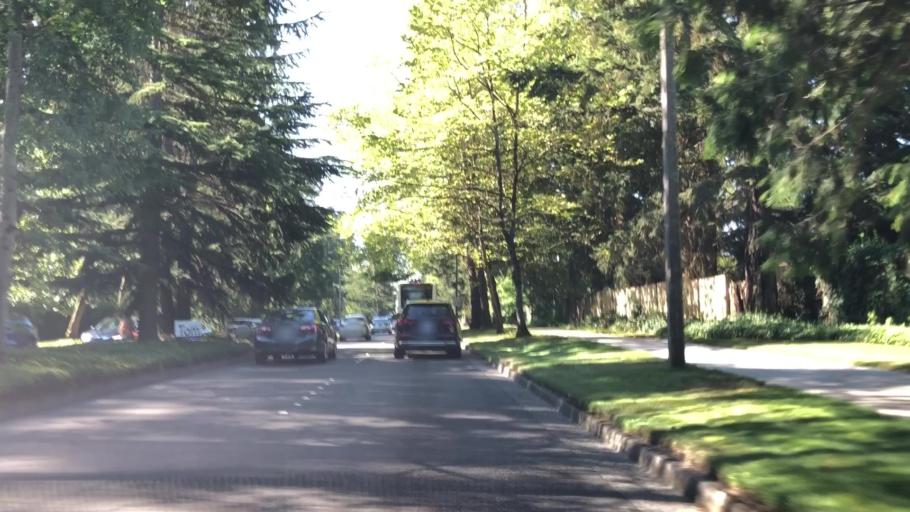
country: US
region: Washington
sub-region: King County
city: Eastgate
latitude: 47.6143
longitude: -122.1431
